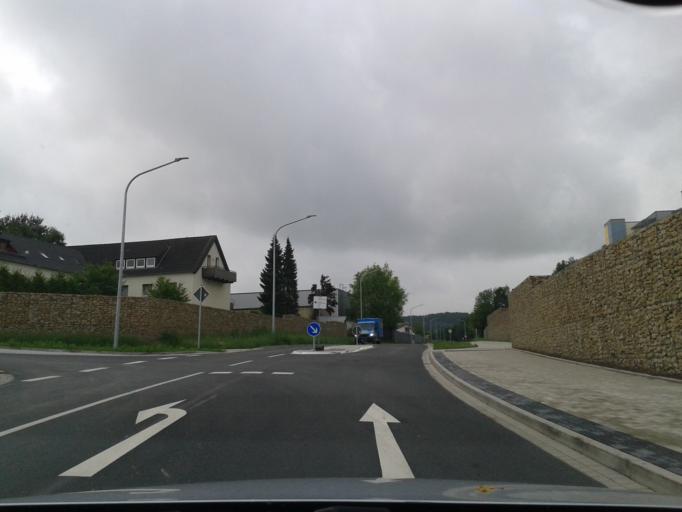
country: DE
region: North Rhine-Westphalia
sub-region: Regierungsbezirk Detmold
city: Lemgo
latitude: 52.0205
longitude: 8.9075
